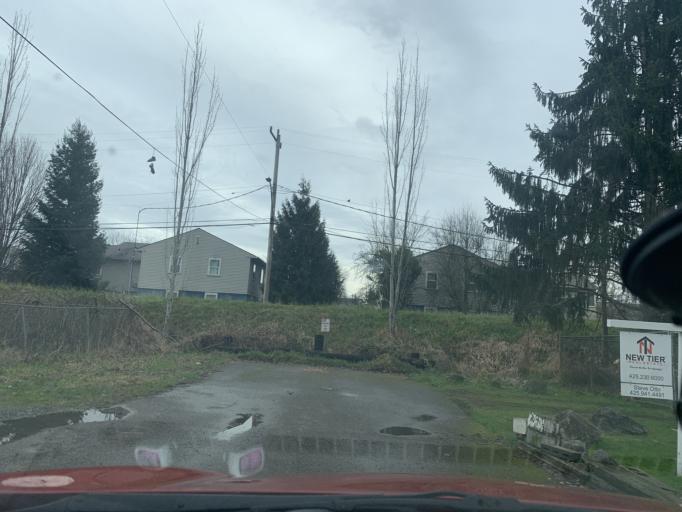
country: US
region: Washington
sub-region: King County
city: Bryn Mawr-Skyway
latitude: 47.5219
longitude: -122.2677
